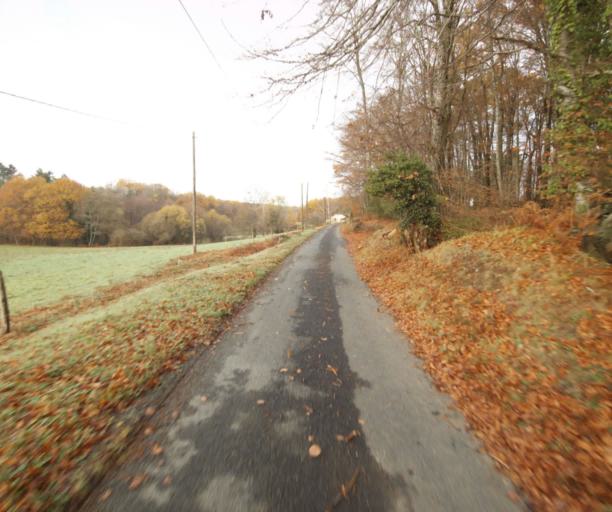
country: FR
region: Limousin
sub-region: Departement de la Correze
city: Cornil
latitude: 45.1979
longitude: 1.7139
